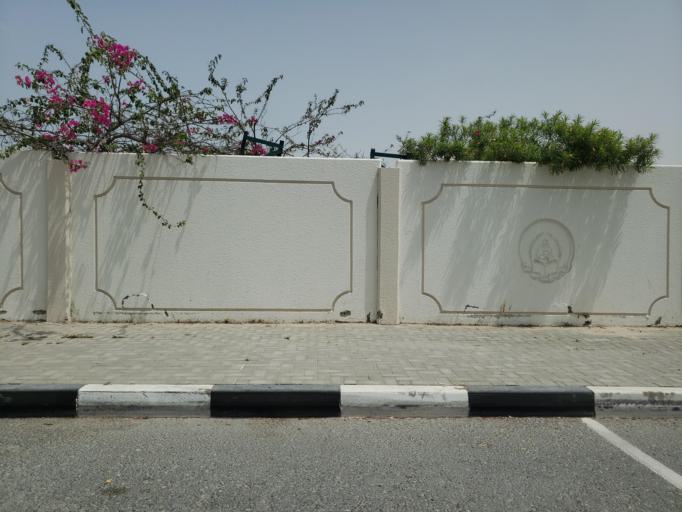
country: AE
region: Ash Shariqah
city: Sharjah
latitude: 25.3467
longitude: 55.4047
